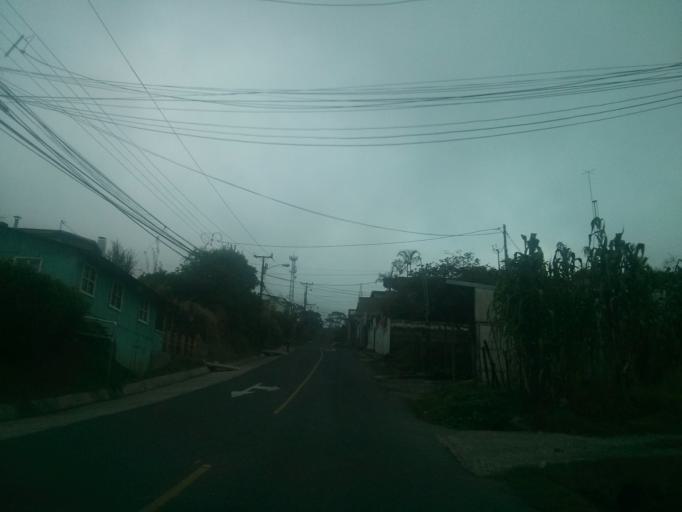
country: CR
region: Cartago
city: Cot
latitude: 9.9136
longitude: -83.8072
